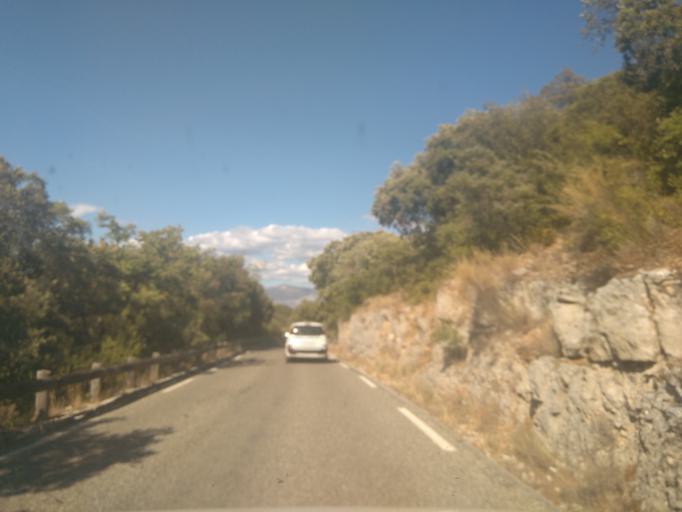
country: FR
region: Provence-Alpes-Cote d'Azur
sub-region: Departement du Var
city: Regusse
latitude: 43.7346
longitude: 6.1304
